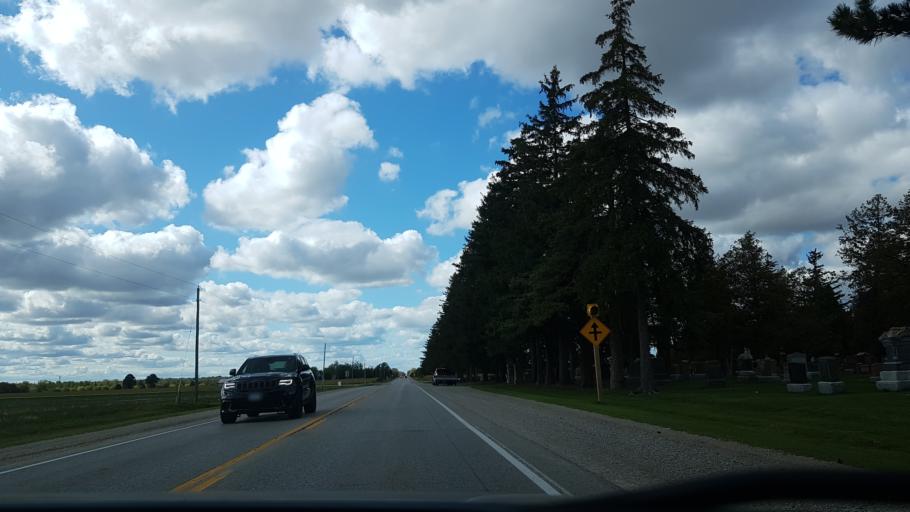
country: CA
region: Ontario
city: South Huron
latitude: 43.3595
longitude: -81.5049
